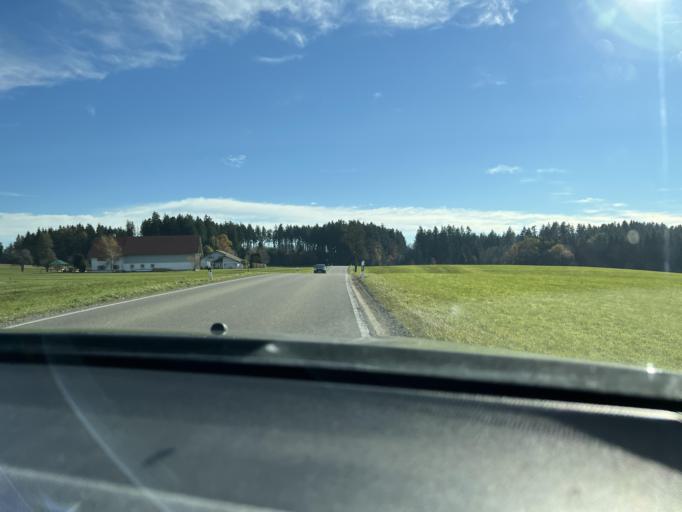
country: DE
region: Bavaria
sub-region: Swabia
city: Gestratz
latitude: 47.7187
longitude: 9.9652
